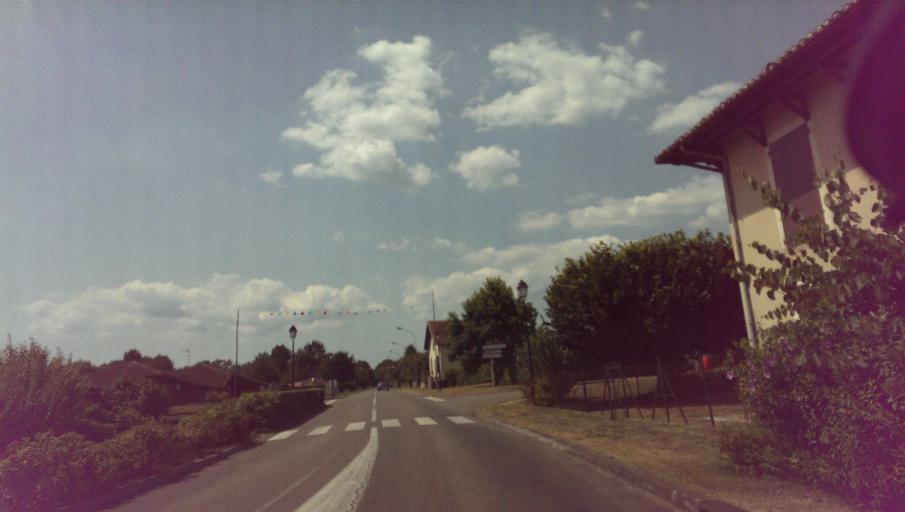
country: FR
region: Aquitaine
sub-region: Departement des Landes
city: Sabres
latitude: 44.1056
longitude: -0.5486
